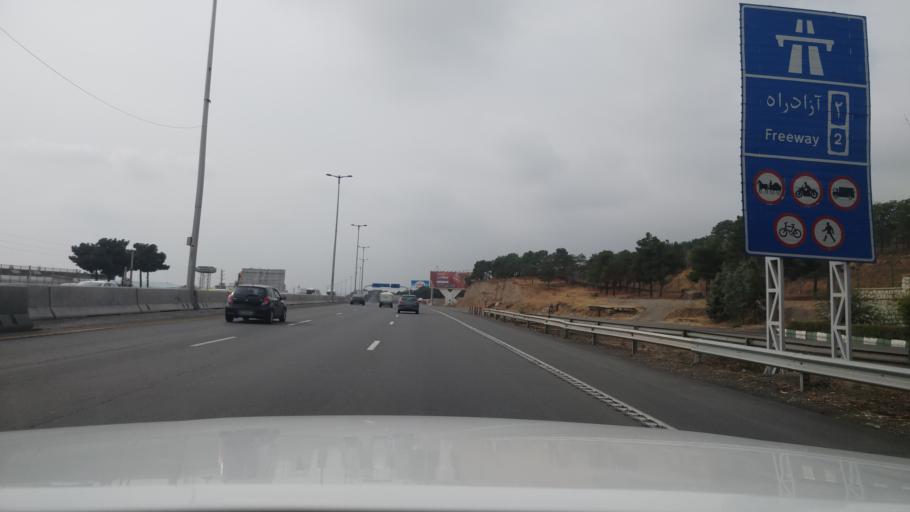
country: IR
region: Tehran
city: Shahr-e Qods
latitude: 35.7172
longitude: 51.2354
